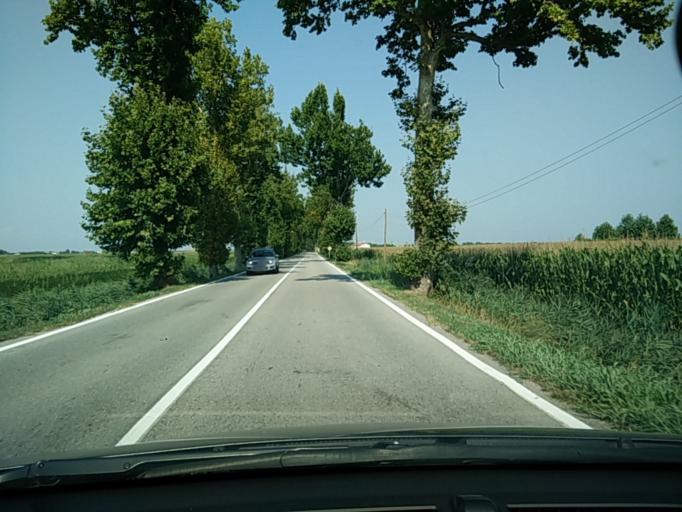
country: IT
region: Veneto
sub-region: Provincia di Venezia
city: San Giorgio di Livenza
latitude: 45.6406
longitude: 12.7555
